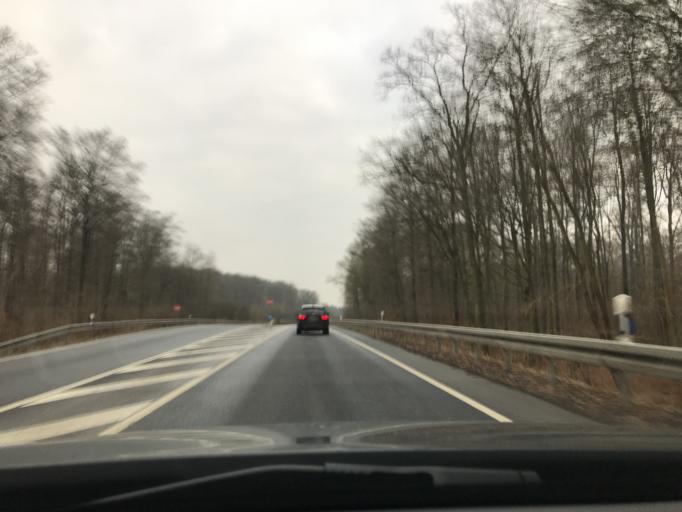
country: DE
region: Hesse
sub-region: Regierungsbezirk Kassel
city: Calden
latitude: 51.3928
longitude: 9.4319
